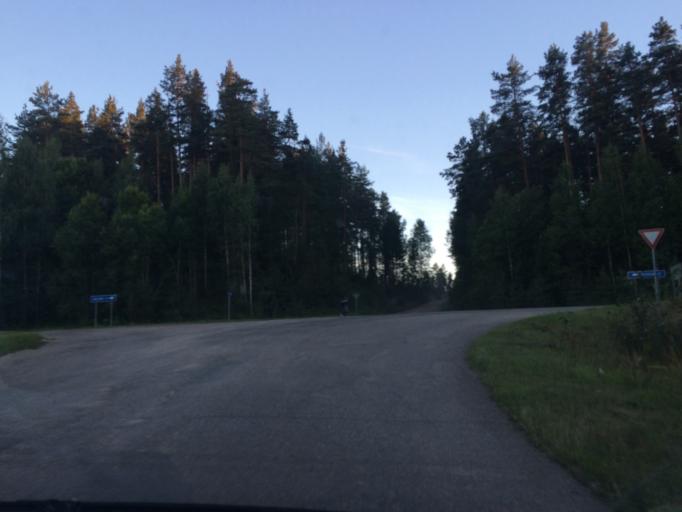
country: LV
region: Aglona
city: Aglona
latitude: 56.1432
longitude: 27.2105
